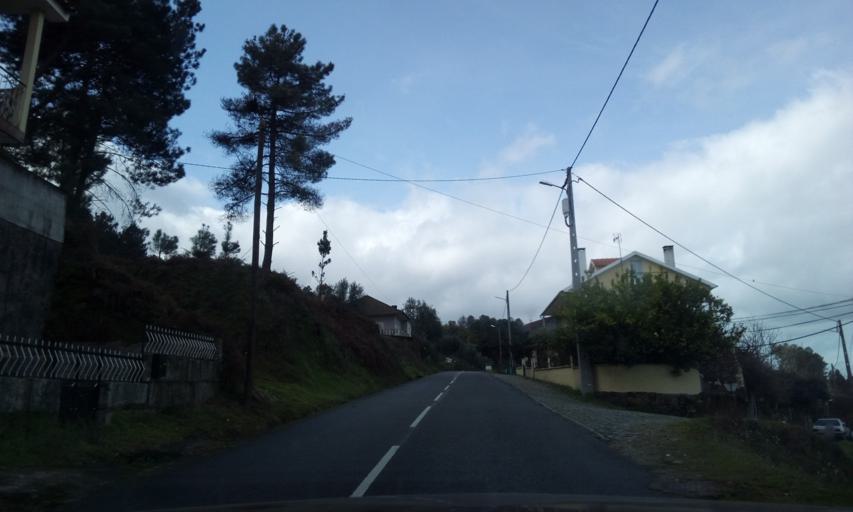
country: PT
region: Guarda
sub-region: Fornos de Algodres
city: Fornos de Algodres
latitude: 40.6608
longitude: -7.6287
